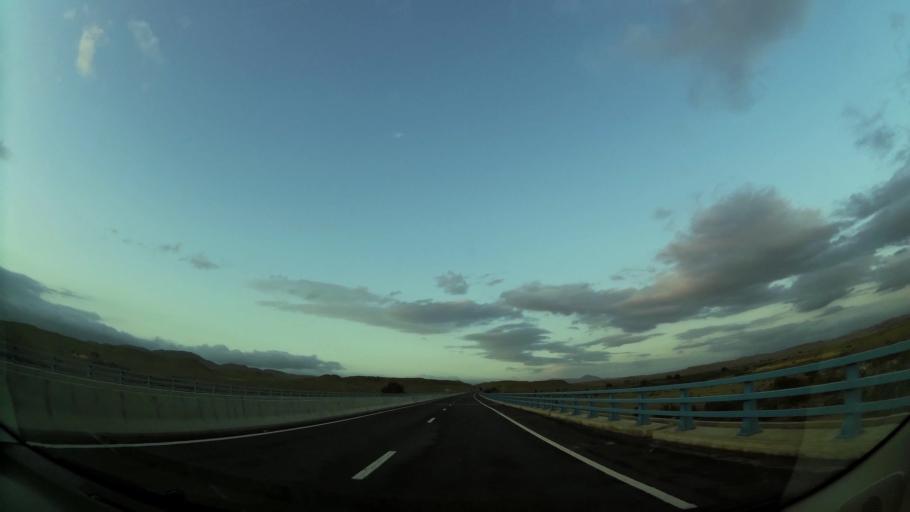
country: MA
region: Oriental
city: Taourirt
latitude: 34.5707
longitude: -2.8235
